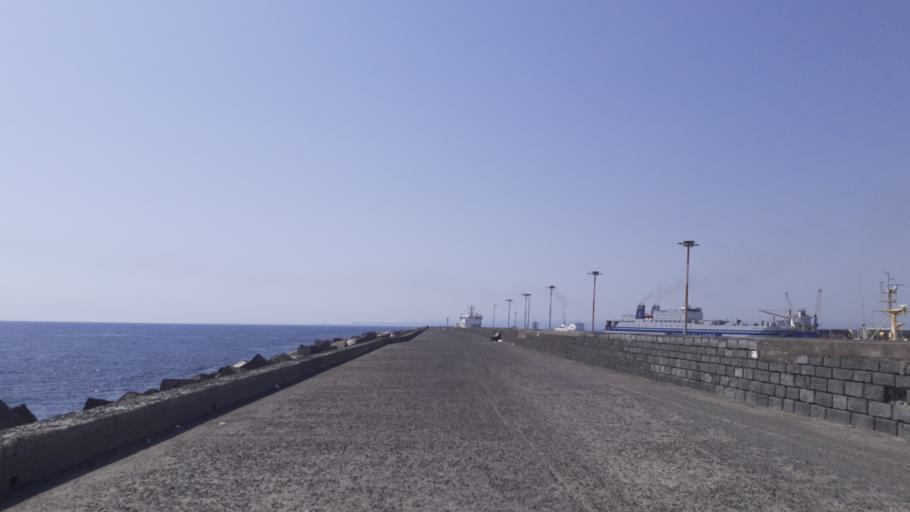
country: IT
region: Sicily
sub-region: Catania
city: Catania
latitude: 37.4997
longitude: 15.0991
